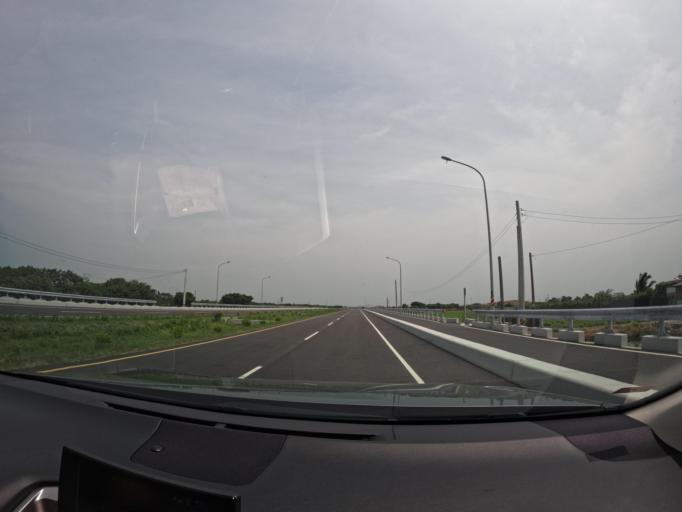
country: TW
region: Taiwan
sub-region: Changhua
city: Chang-hua
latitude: 23.9366
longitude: 120.3362
